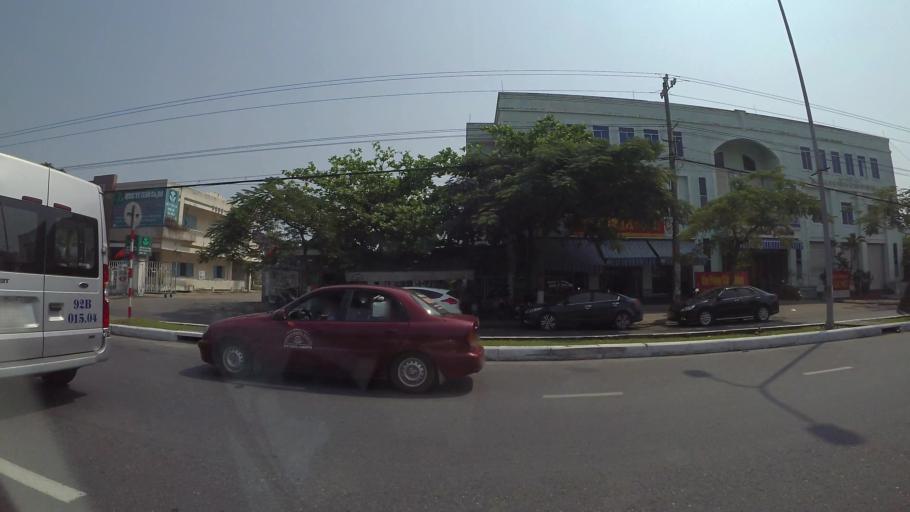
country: VN
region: Da Nang
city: Son Tra
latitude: 16.0506
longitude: 108.2377
